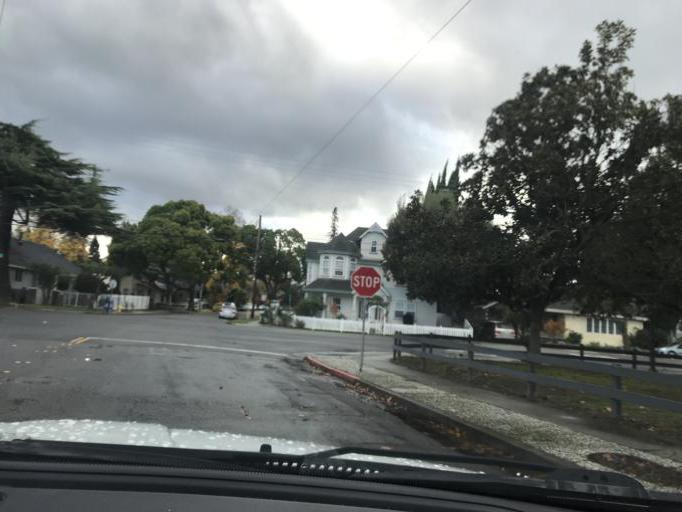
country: US
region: California
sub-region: Santa Clara County
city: Buena Vista
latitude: 37.3015
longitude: -121.9042
